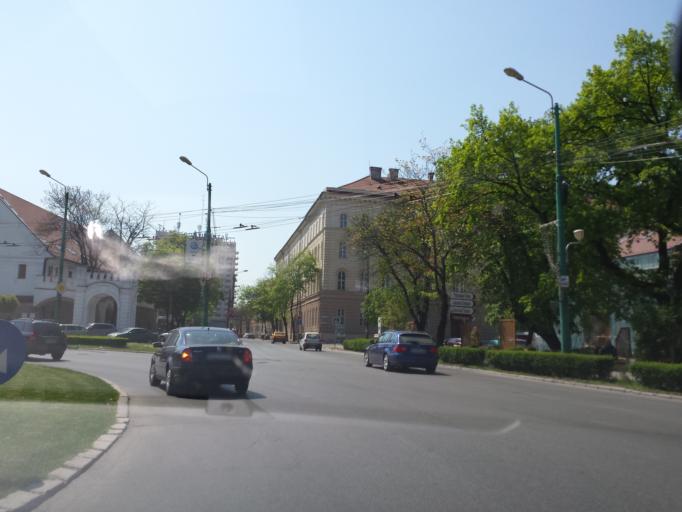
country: RO
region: Timis
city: Timisoara
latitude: 45.7581
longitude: 21.2324
